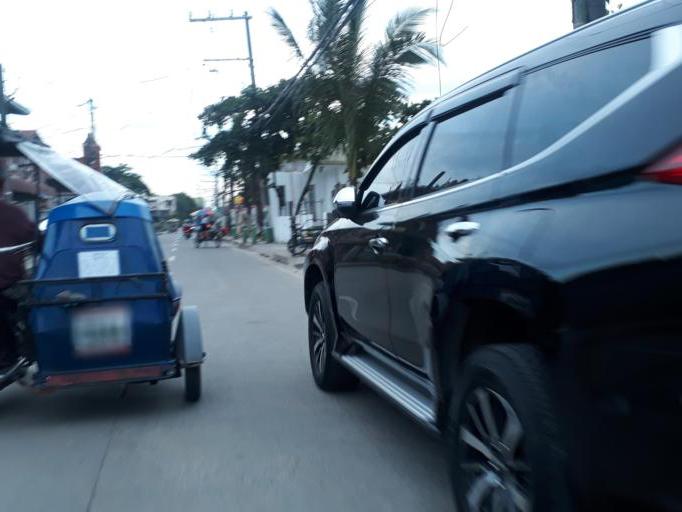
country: PH
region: Central Luzon
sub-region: Province of Bulacan
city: Obando
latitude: 14.7096
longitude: 120.9518
